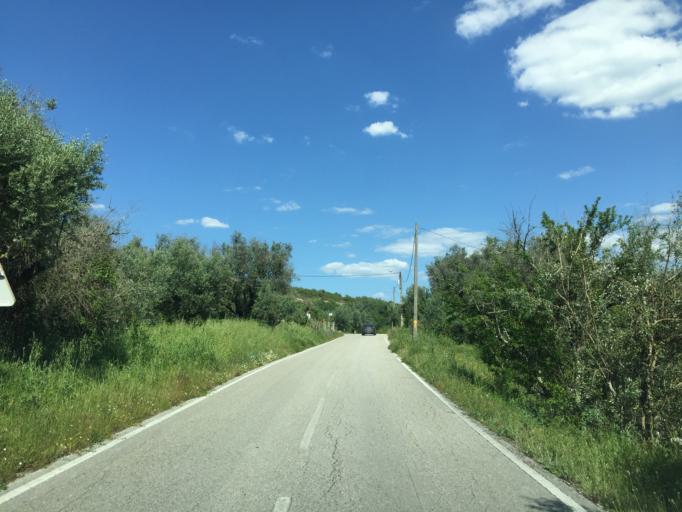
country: PT
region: Leiria
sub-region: Alvaiazere
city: Alvaiazere
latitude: 39.8032
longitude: -8.4097
